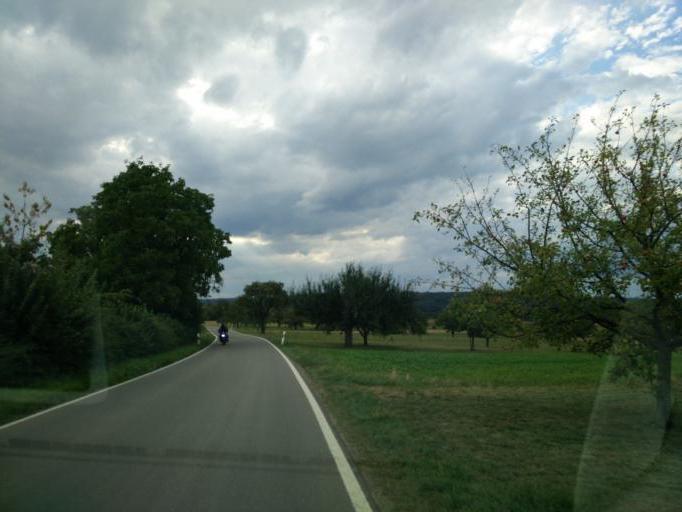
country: DE
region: Baden-Wuerttemberg
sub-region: Tuebingen Region
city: Sickenhausen
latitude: 48.5344
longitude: 9.1684
